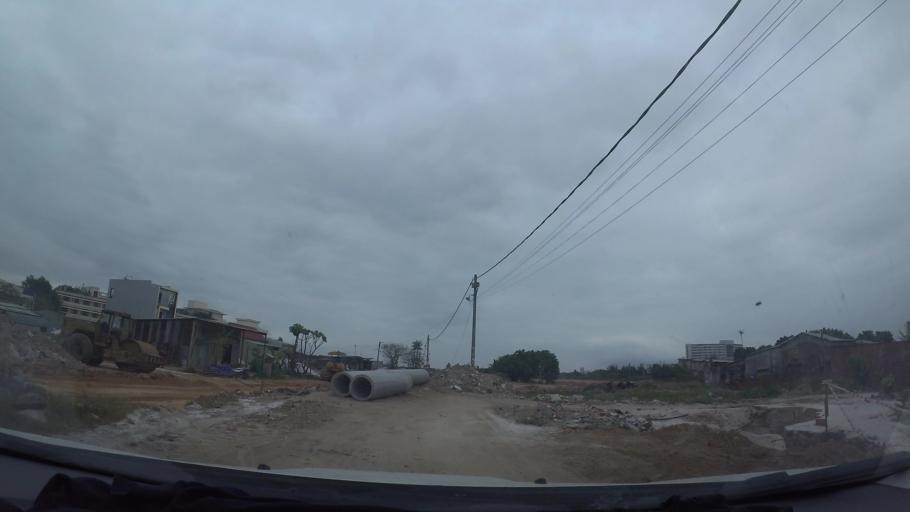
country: VN
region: Da Nang
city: Lien Chieu
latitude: 16.0669
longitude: 108.1592
